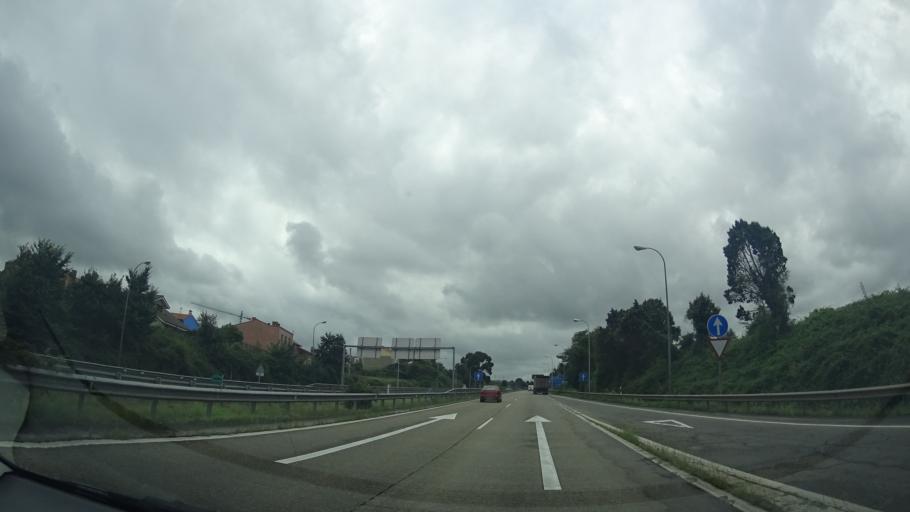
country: ES
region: Asturias
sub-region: Province of Asturias
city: Natahoyo
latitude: 43.5309
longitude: -5.6842
